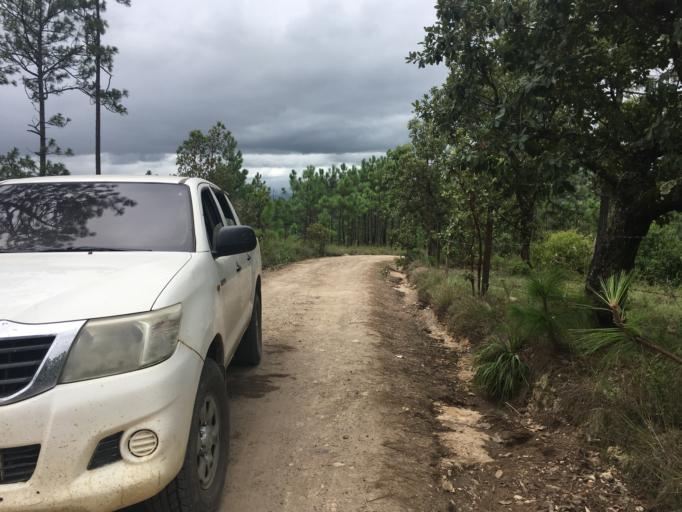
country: GT
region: Totonicapan
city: Santa Lucia La Reforma
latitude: 15.0949
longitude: -91.2135
